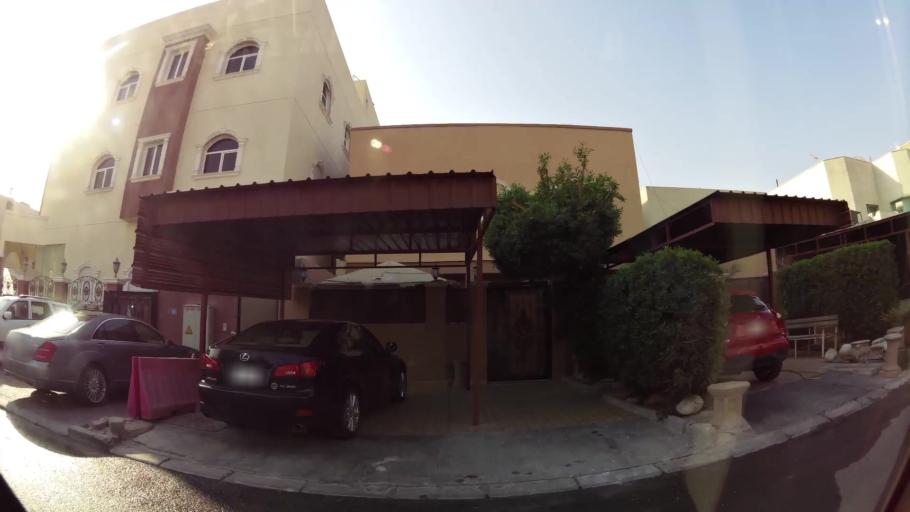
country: KW
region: Al Asimah
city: Ad Dasmah
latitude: 29.3681
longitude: 48.0007
